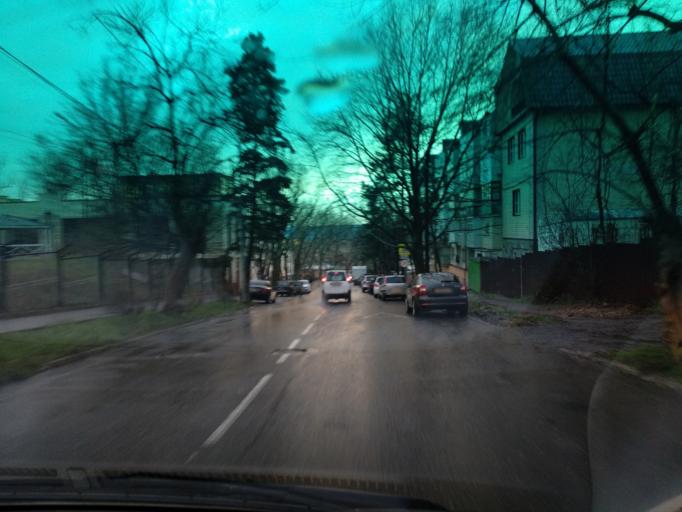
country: RU
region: Krasnodarskiy
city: Tuapse
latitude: 44.1020
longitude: 39.0816
